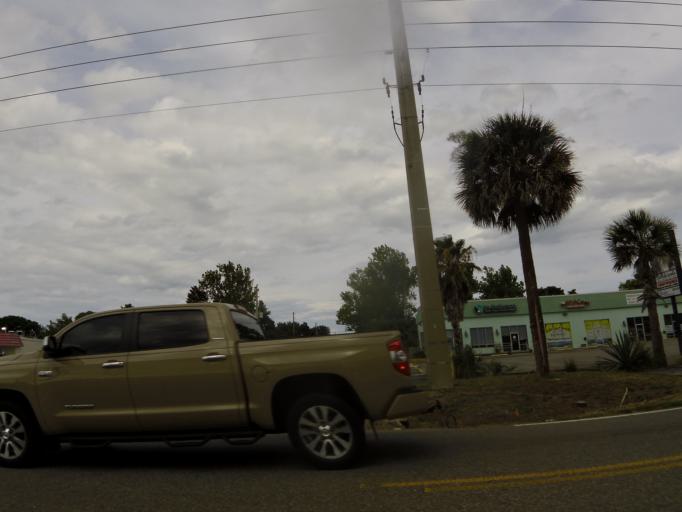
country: US
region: Florida
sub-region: Duval County
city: Neptune Beach
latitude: 30.3023
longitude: -81.4066
